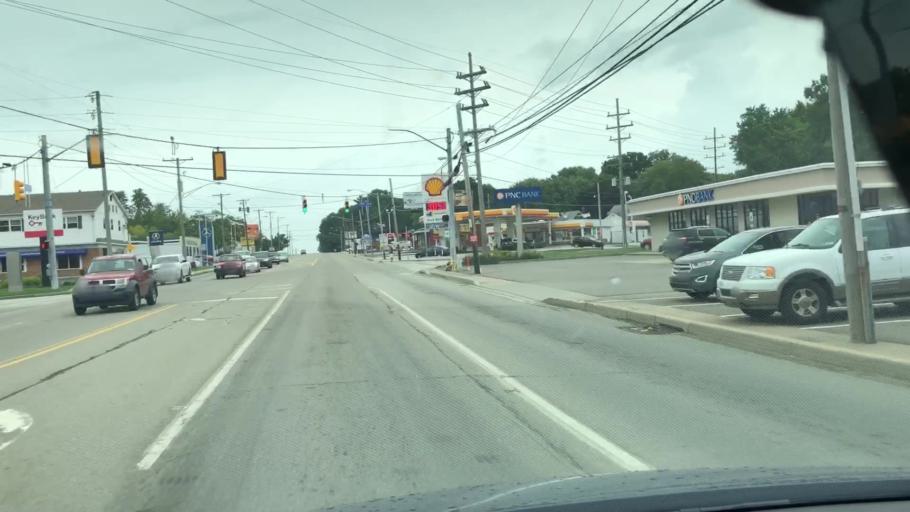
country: US
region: Pennsylvania
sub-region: Erie County
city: Erie
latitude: 42.0810
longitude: -80.0902
